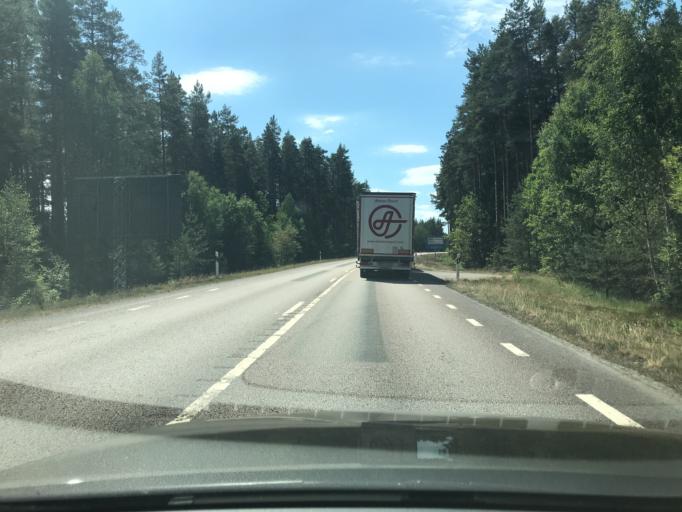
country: SE
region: Kalmar
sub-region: Hultsfreds Kommun
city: Malilla
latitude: 57.3859
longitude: 15.7537
